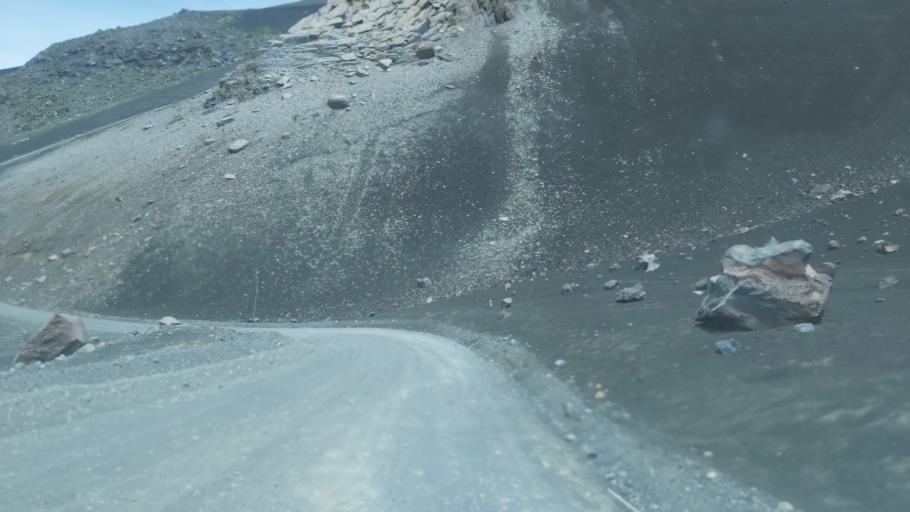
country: AR
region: Neuquen
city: Andacollo
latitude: -37.4051
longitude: -71.3008
